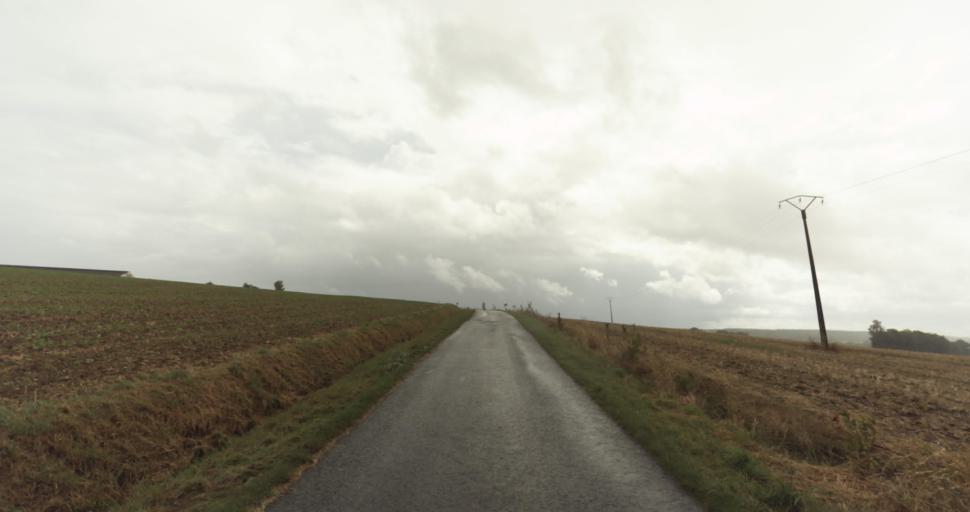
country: FR
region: Lower Normandy
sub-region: Departement de l'Orne
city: Sainte-Gauburge-Sainte-Colombe
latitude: 48.6974
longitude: 0.4069
